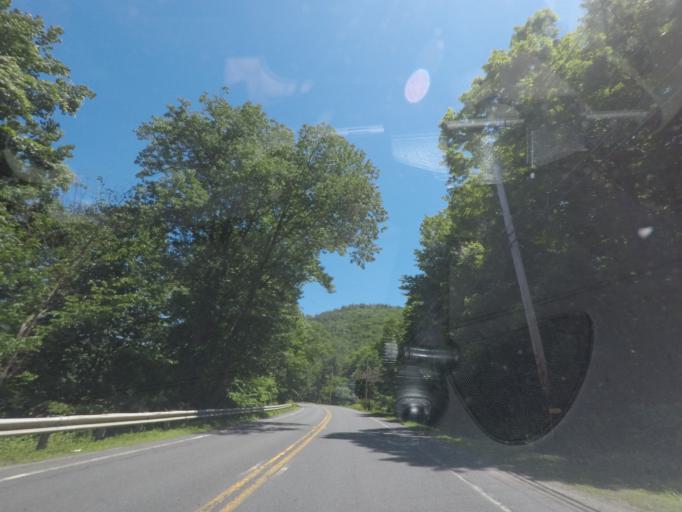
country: US
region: Massachusetts
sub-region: Berkshire County
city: Becket
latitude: 42.2569
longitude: -72.9500
